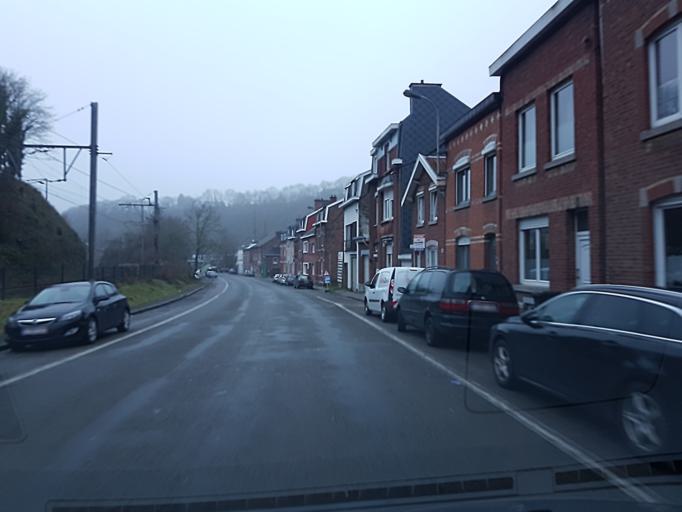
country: BE
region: Wallonia
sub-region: Province de Liege
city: Pepinster
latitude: 50.5614
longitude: 5.8120
